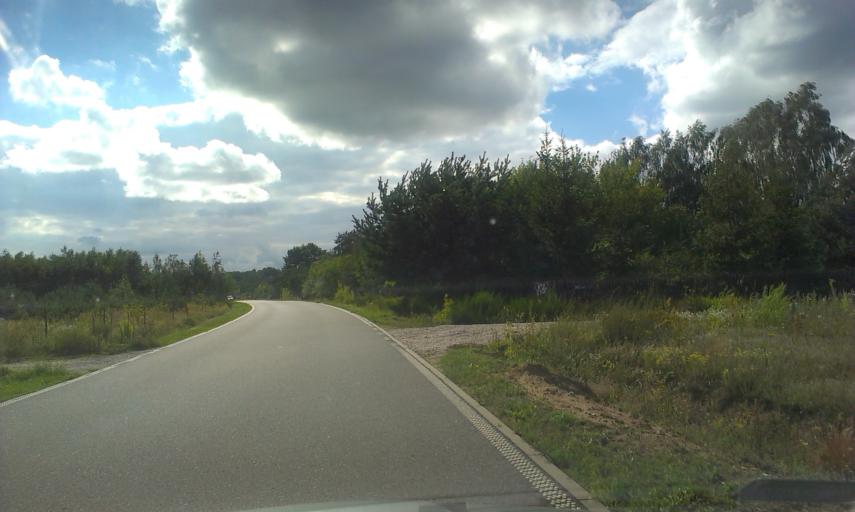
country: PL
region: Masovian Voivodeship
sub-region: Powiat zyrardowski
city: Radziejowice
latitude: 51.9682
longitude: 20.6265
